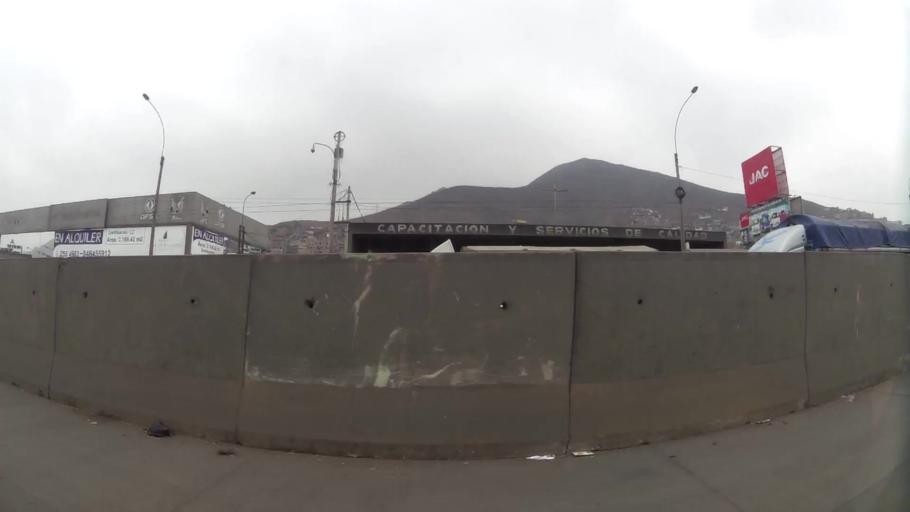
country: PE
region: Lima
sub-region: Lima
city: San Luis
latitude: -12.0635
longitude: -76.9854
